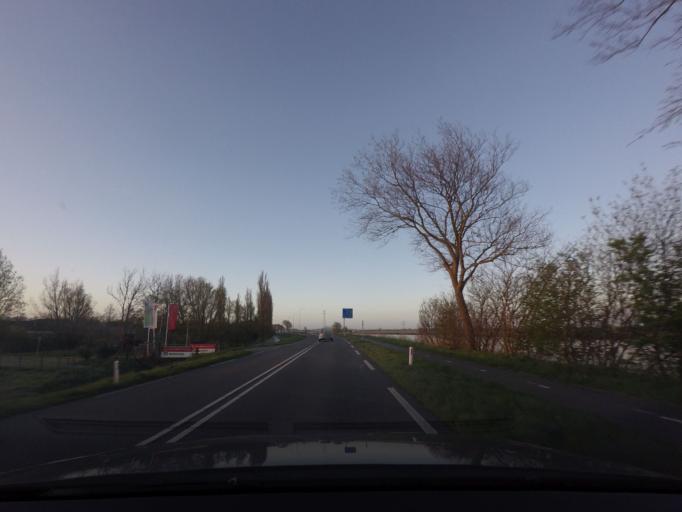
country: NL
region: North Holland
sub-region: Gemeente Uitgeest
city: Uitgeest
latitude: 52.5327
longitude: 4.7779
